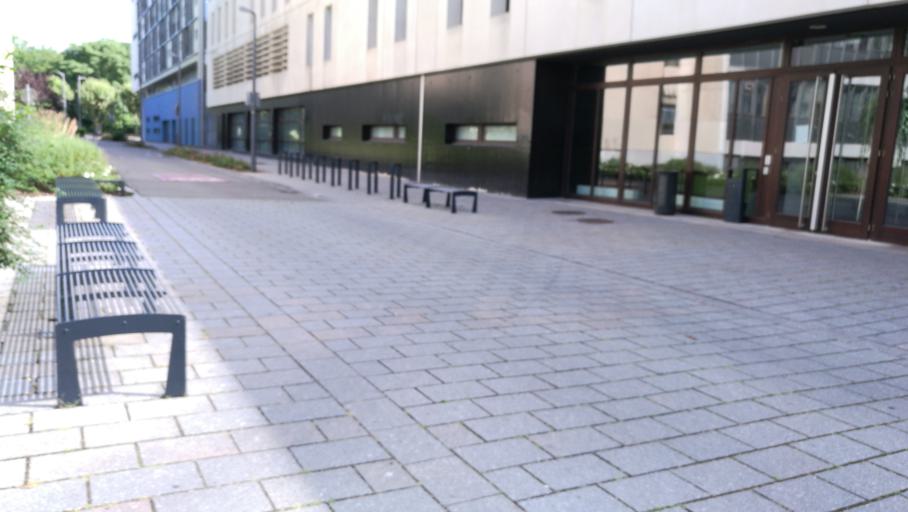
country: FR
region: Alsace
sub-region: Departement du Bas-Rhin
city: Strasbourg
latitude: 48.5803
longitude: 7.7679
